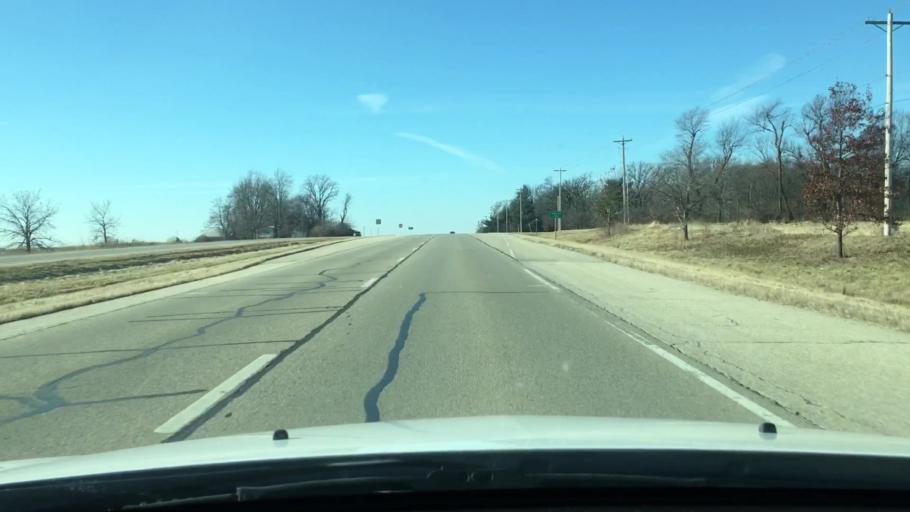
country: US
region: Illinois
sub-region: Woodford County
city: Metamora
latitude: 40.7799
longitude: -89.4068
